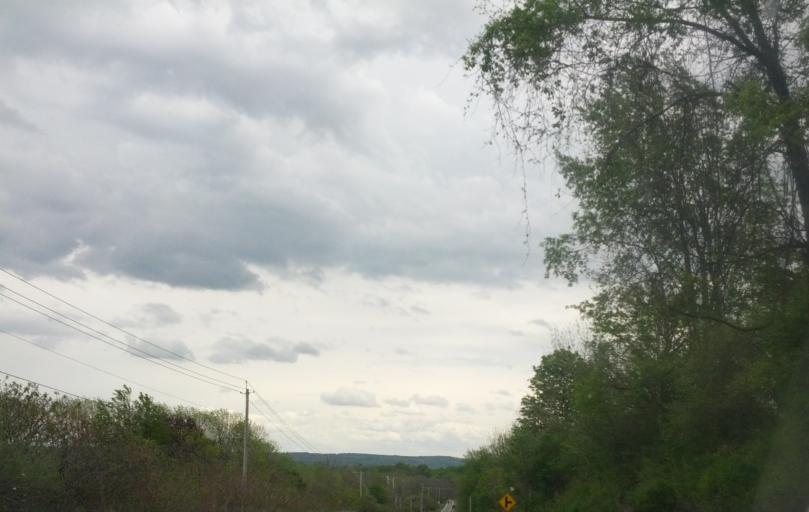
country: US
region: New York
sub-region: Onondaga County
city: Fayetteville
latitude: 42.9917
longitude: -76.0226
